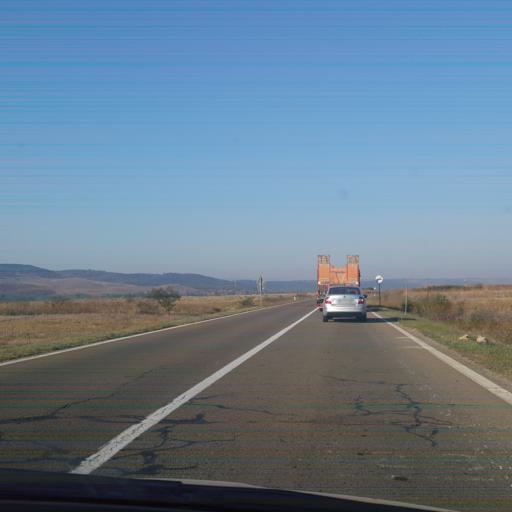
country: RS
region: Central Serbia
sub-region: Nisavski Okrug
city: Merosina
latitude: 43.2791
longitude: 21.7971
